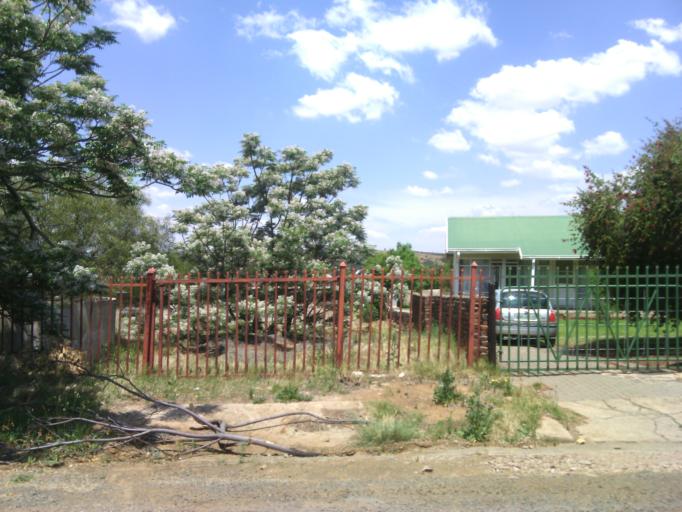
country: ZA
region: Orange Free State
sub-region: Xhariep District Municipality
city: Dewetsdorp
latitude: -29.5797
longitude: 26.6638
